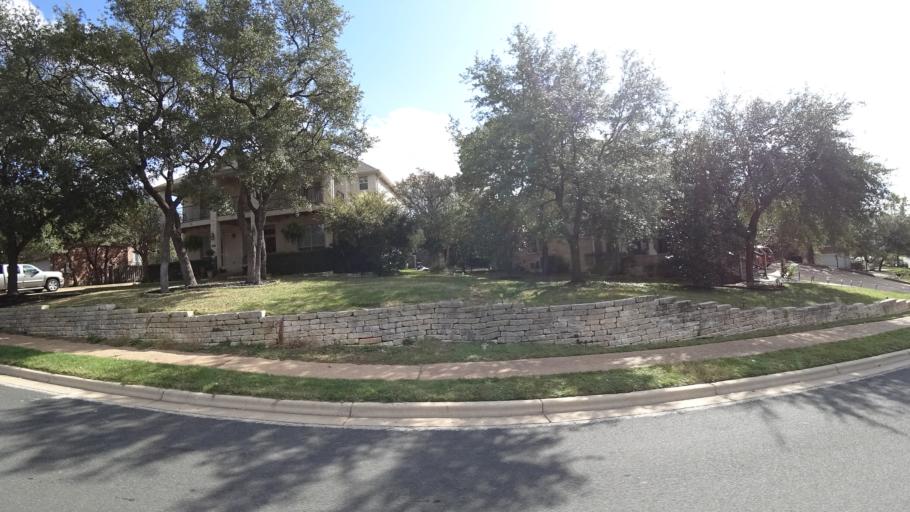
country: US
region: Texas
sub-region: Williamson County
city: Anderson Mill
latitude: 30.4286
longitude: -97.8118
